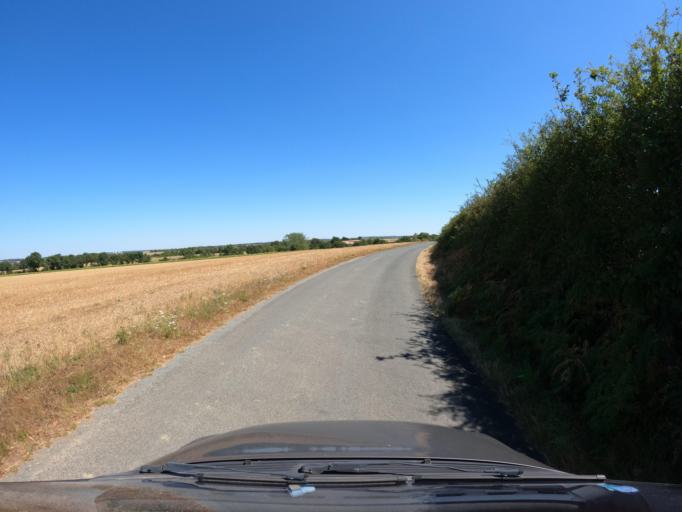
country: FR
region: Pays de la Loire
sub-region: Departement de Maine-et-Loire
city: La Seguiniere
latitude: 47.0520
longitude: -0.9673
